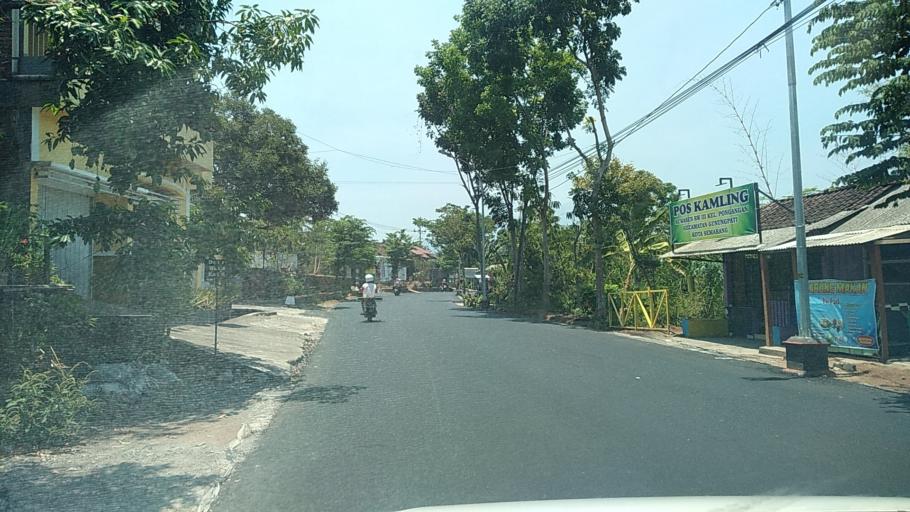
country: ID
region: Central Java
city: Semarang
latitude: -7.0517
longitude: 110.3590
